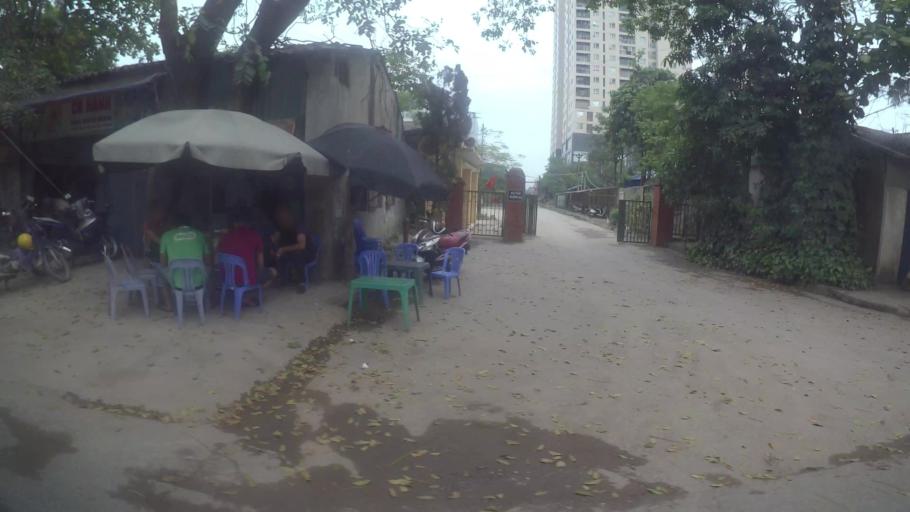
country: VN
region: Ha Noi
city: Cau Dien
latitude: 21.0170
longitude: 105.7450
